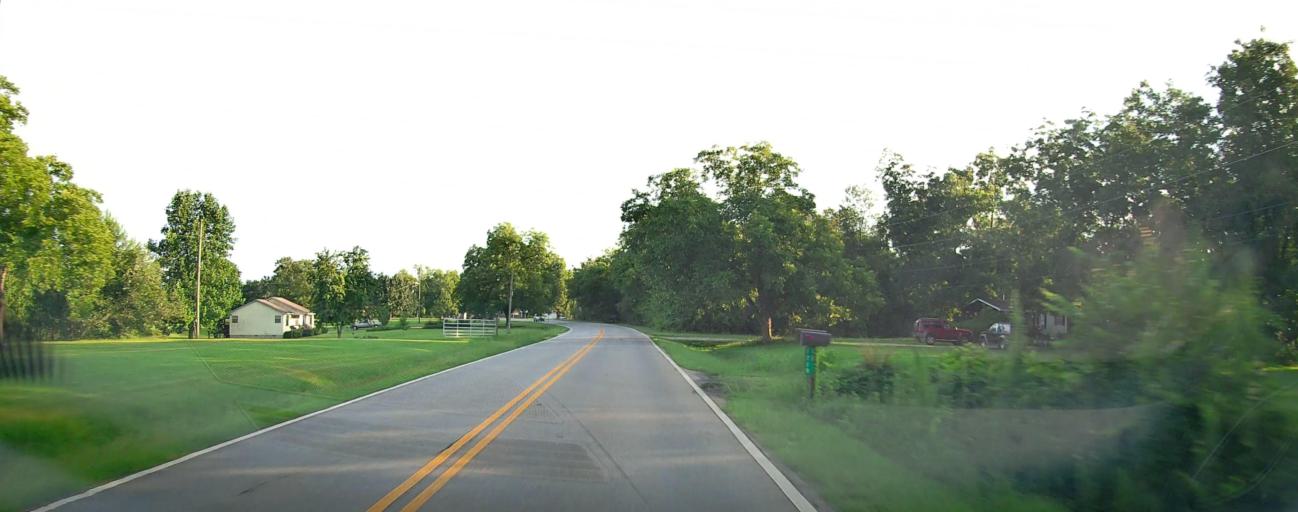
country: US
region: Georgia
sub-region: Peach County
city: Fort Valley
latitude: 32.5885
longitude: -83.8732
